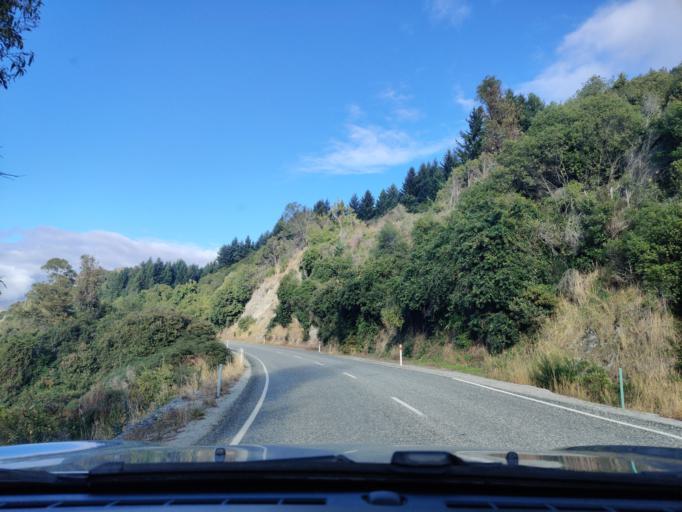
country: NZ
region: Otago
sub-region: Queenstown-Lakes District
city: Queenstown
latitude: -45.0475
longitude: 168.6229
